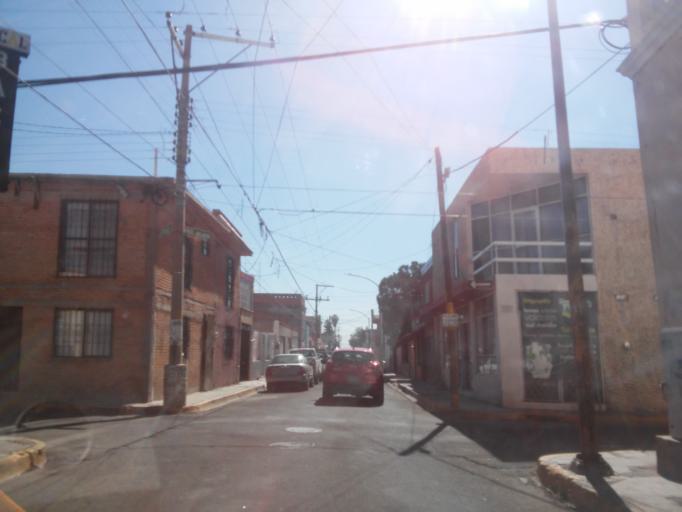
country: MX
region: Durango
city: Victoria de Durango
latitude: 24.0320
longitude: -104.6642
